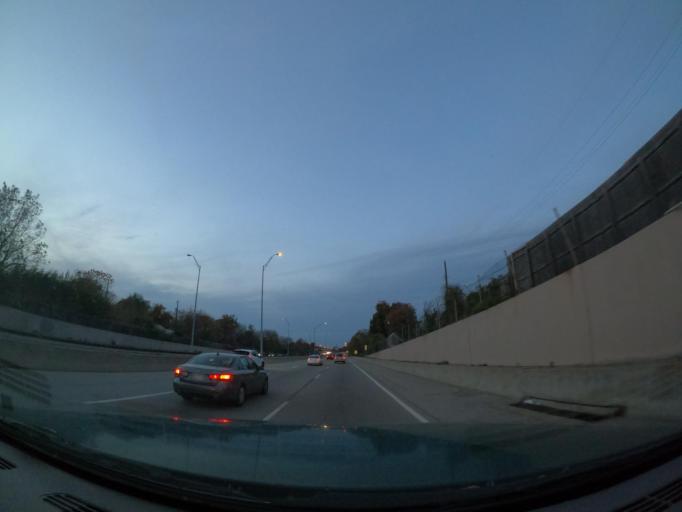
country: US
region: Oklahoma
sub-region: Tulsa County
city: Tulsa
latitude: 36.1360
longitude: -95.9508
